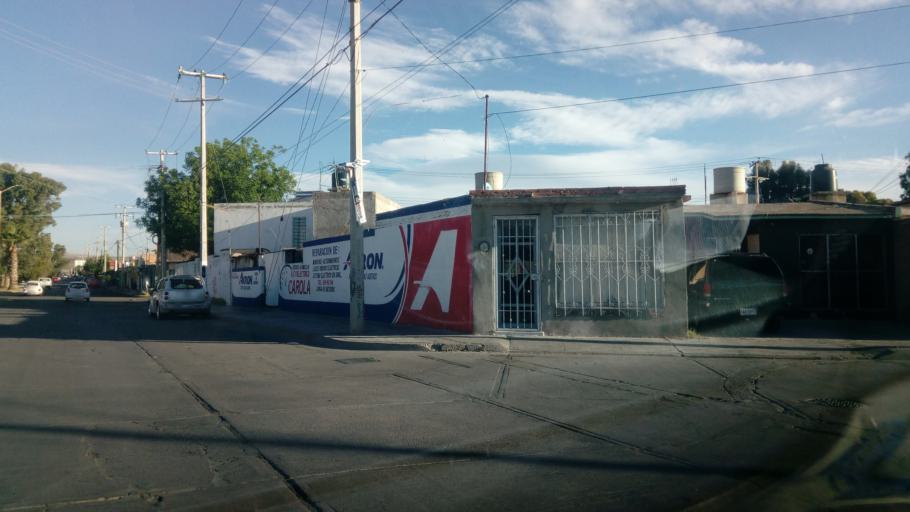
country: MX
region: Durango
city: Victoria de Durango
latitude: 24.0616
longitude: -104.5950
